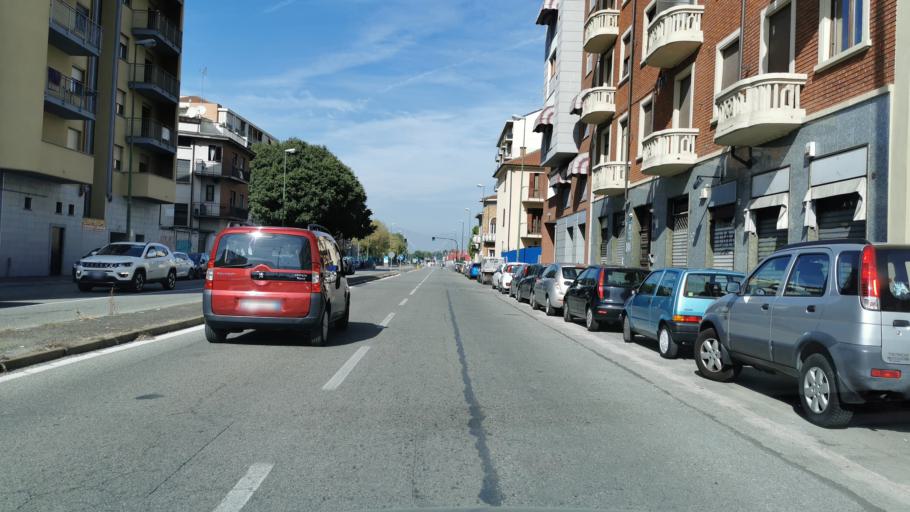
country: IT
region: Piedmont
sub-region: Provincia di Torino
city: Venaria Reale
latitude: 45.1069
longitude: 7.6633
